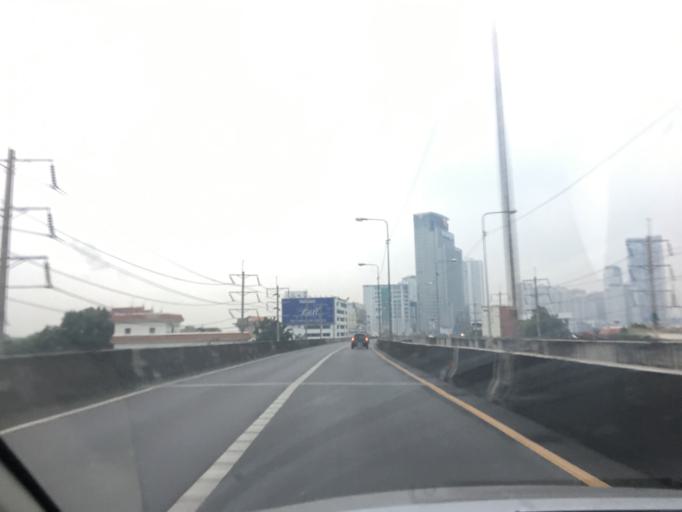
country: TH
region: Bangkok
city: Yan Nawa
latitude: 13.6834
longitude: 100.5480
